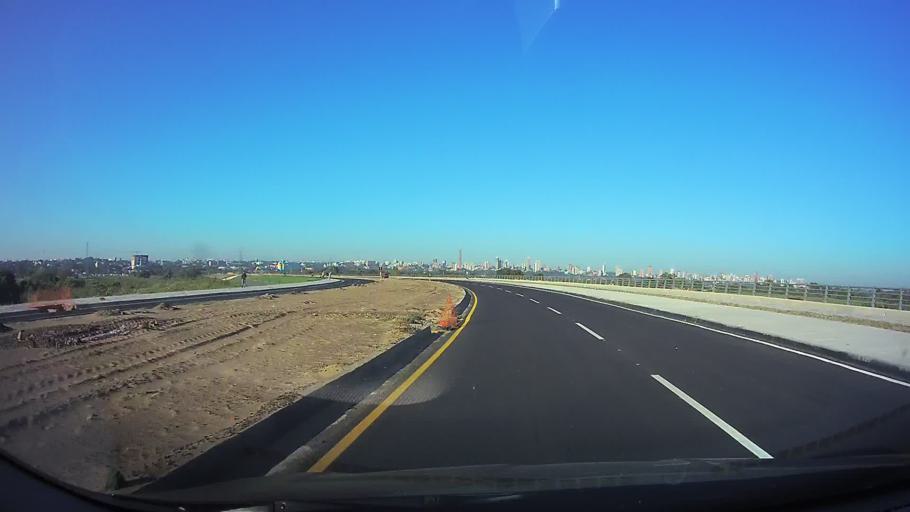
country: PY
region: Asuncion
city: Asuncion
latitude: -25.2556
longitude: -57.6078
